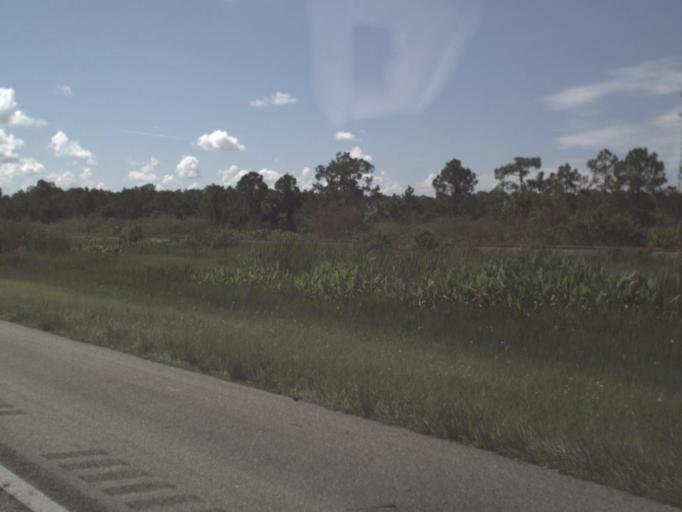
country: US
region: Florida
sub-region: Lee County
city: Suncoast Estates
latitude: 26.8143
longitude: -81.9364
